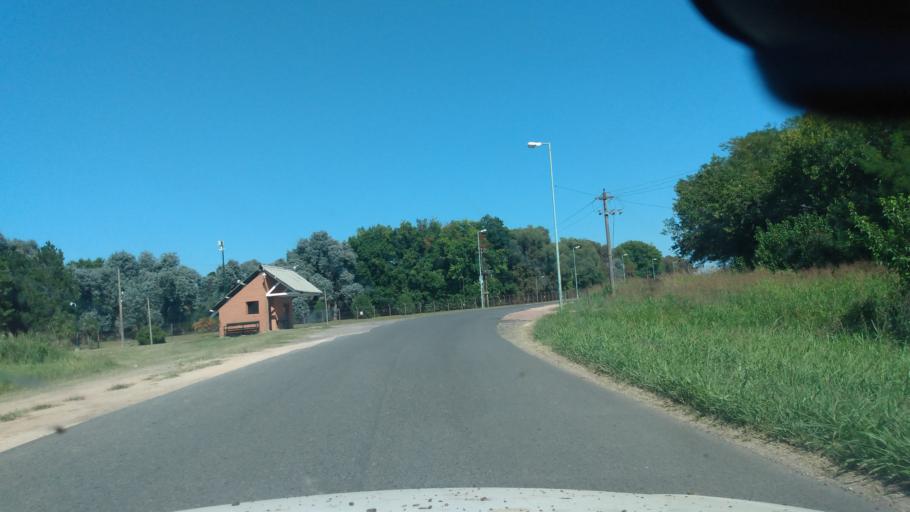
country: AR
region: Buenos Aires
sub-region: Partido de Lujan
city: Lujan
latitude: -34.5096
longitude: -59.0862
